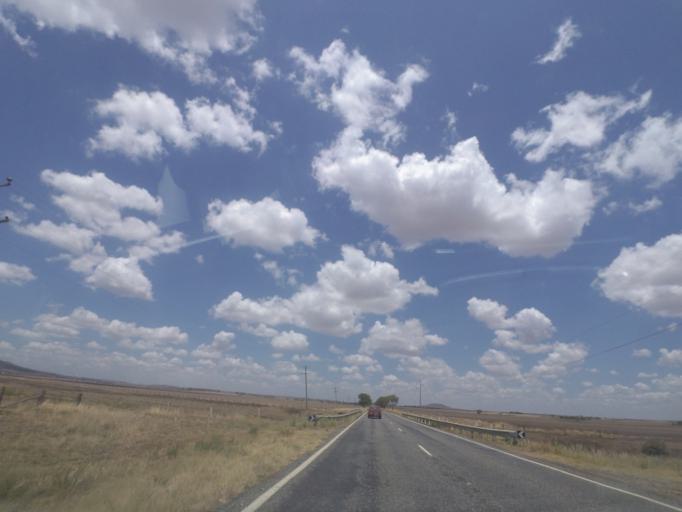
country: AU
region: Queensland
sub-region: Toowoomba
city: Top Camp
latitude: -27.9128
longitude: 151.9802
